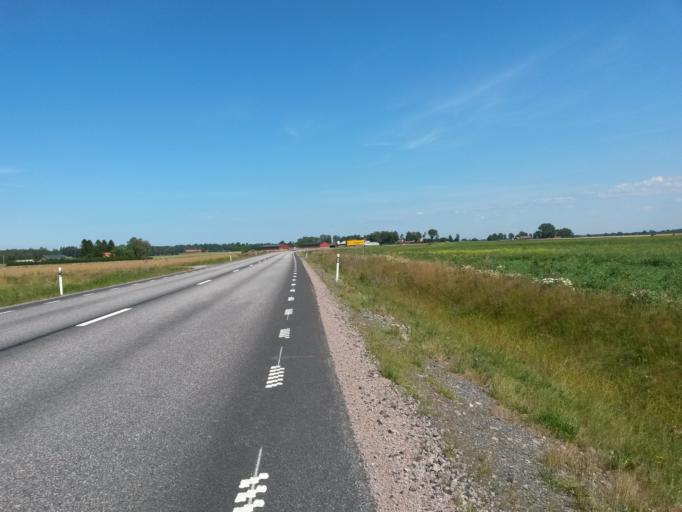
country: SE
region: Vaestra Goetaland
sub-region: Lidkopings Kommun
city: Lidkoping
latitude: 58.4766
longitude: 13.0760
